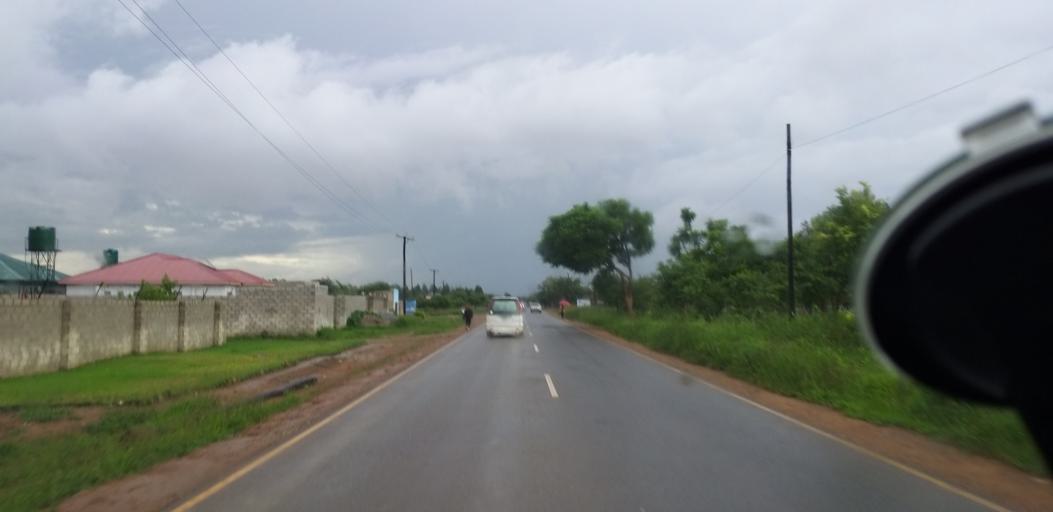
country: ZM
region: Lusaka
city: Lusaka
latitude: -15.4820
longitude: 28.3154
